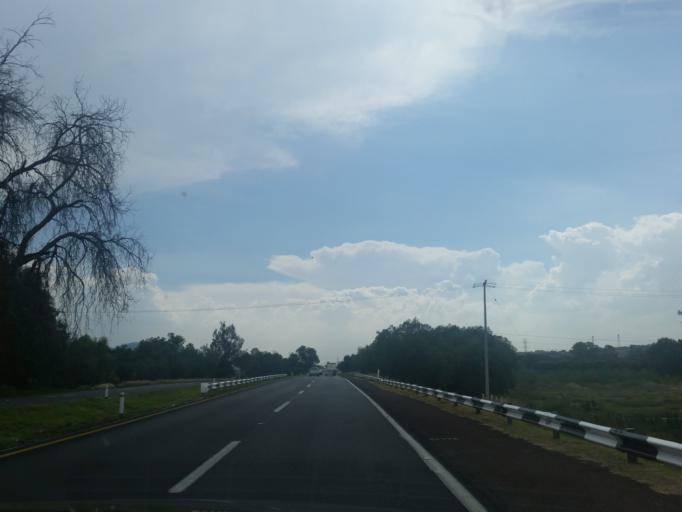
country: MX
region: Mexico
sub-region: Acolman de Nezahualcoyotl
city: Prados de San Juan
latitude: 19.6209
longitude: -98.9619
